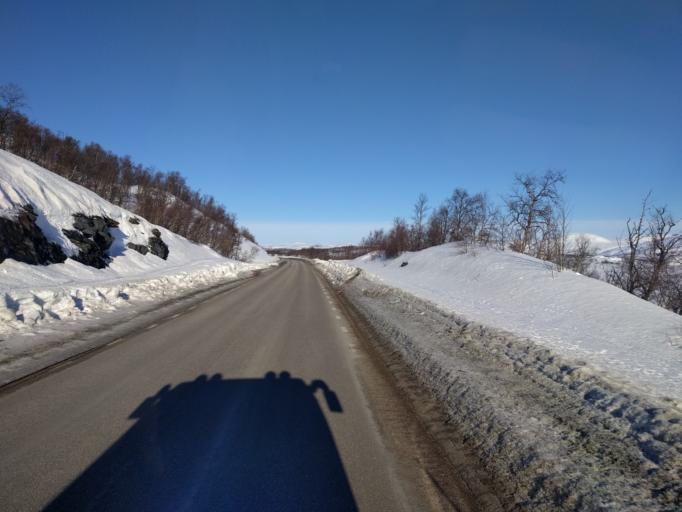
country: NO
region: Troms
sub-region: Bardu
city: Setermoen
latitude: 68.4325
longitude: 18.6664
